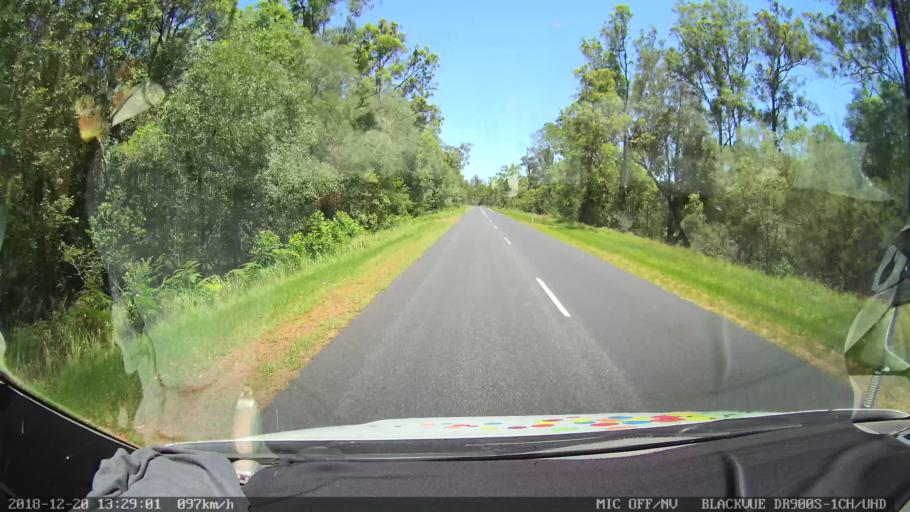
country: AU
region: New South Wales
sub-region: Clarence Valley
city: Gordon
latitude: -29.1831
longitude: 152.9891
